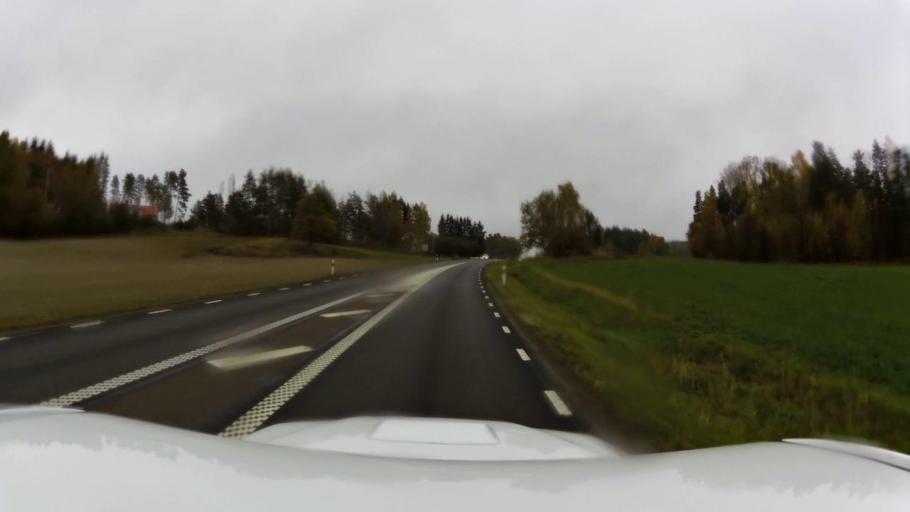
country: SE
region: OEstergoetland
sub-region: Linkopings Kommun
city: Linghem
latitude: 58.3708
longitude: 15.8167
